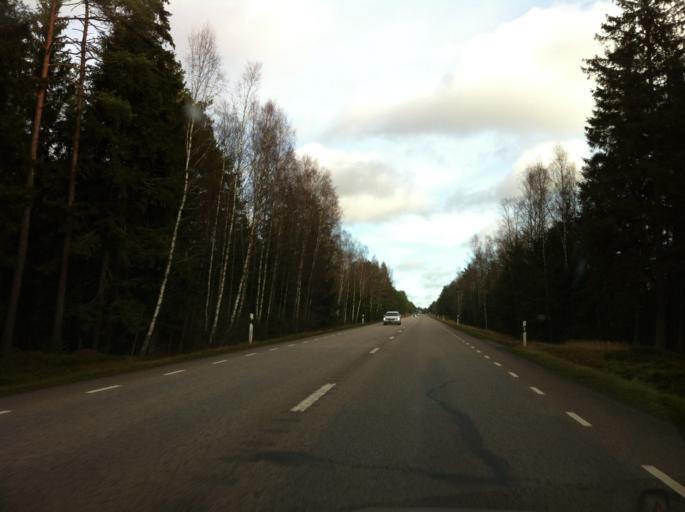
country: SE
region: Kronoberg
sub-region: Uppvidinge Kommun
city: Lenhovda
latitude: 57.0987
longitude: 15.2032
